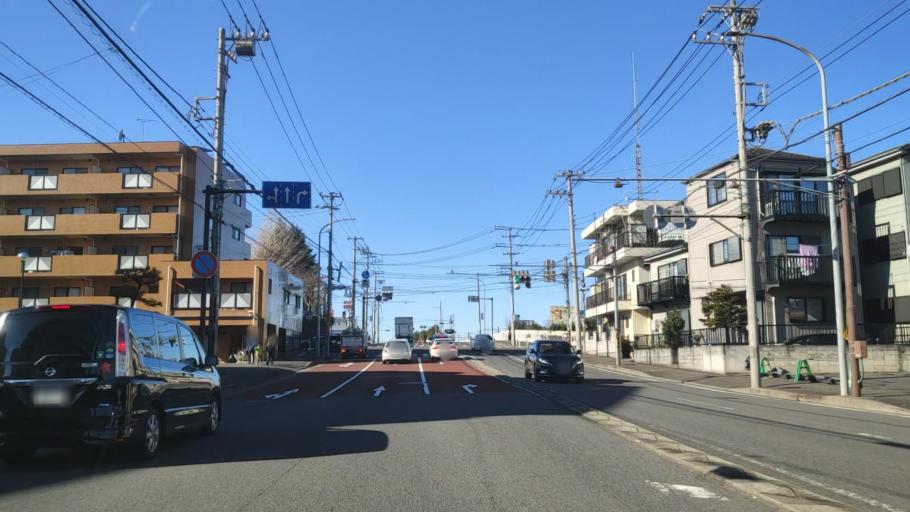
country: JP
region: Tokyo
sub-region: Machida-shi
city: Machida
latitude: 35.5162
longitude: 139.5349
